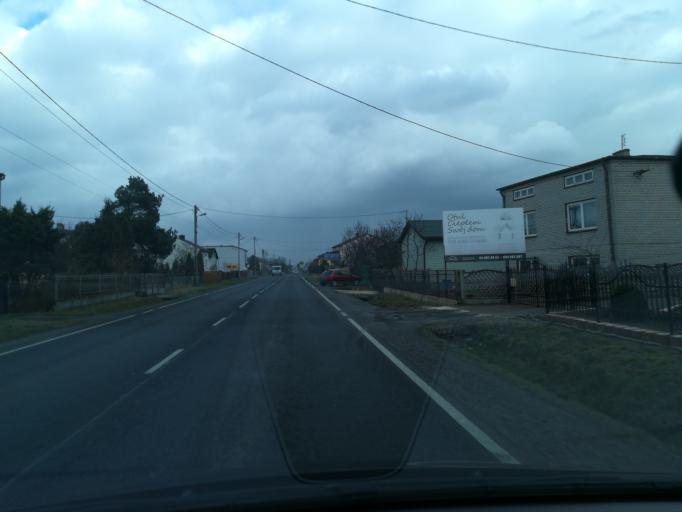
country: PL
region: Lodz Voivodeship
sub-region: Powiat radomszczanski
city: Radomsko
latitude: 51.0785
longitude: 19.3839
